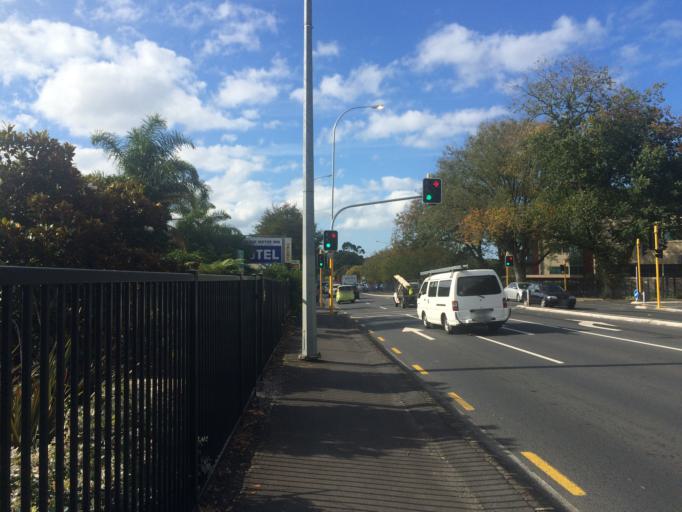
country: NZ
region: Auckland
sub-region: Auckland
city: Auckland
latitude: -36.8877
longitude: 174.7991
